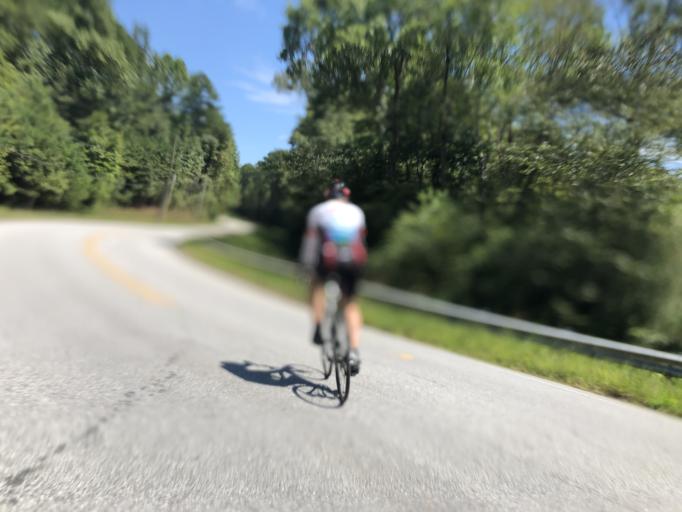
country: US
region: Georgia
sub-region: Fulton County
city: Chattahoochee Hills
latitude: 33.4792
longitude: -84.8084
